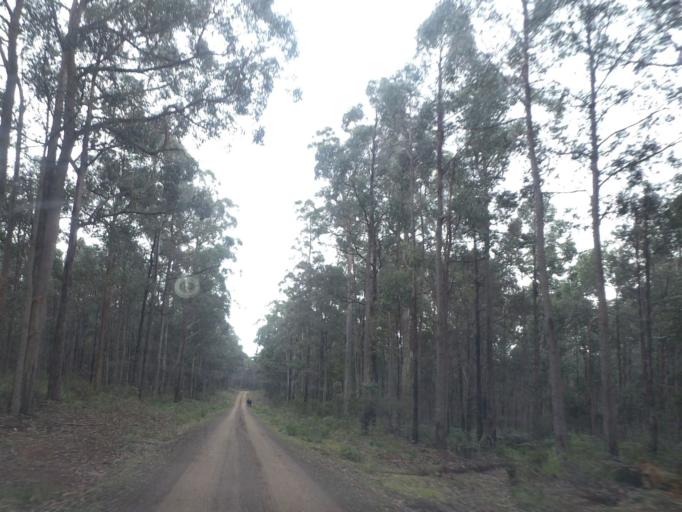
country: AU
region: Victoria
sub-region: Moorabool
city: Bacchus Marsh
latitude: -37.4235
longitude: 144.3100
